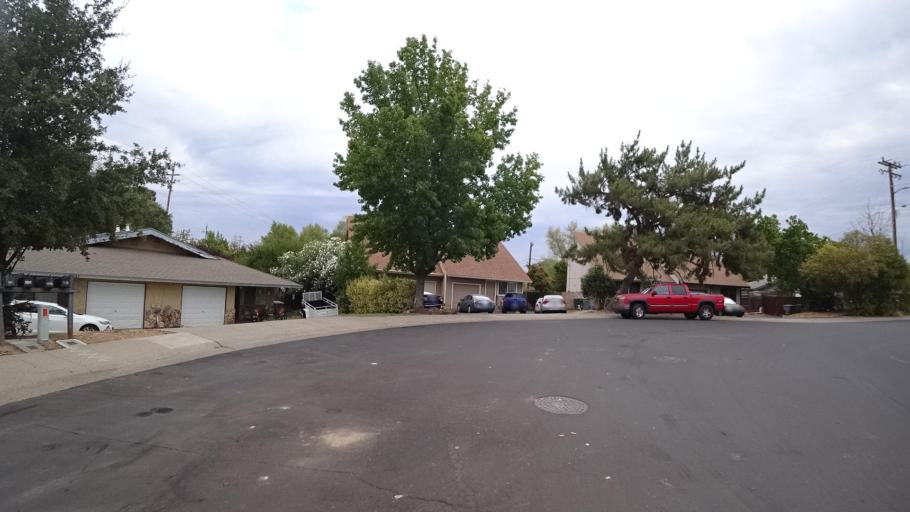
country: US
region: California
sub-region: Placer County
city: Rocklin
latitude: 38.7779
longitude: -121.2456
